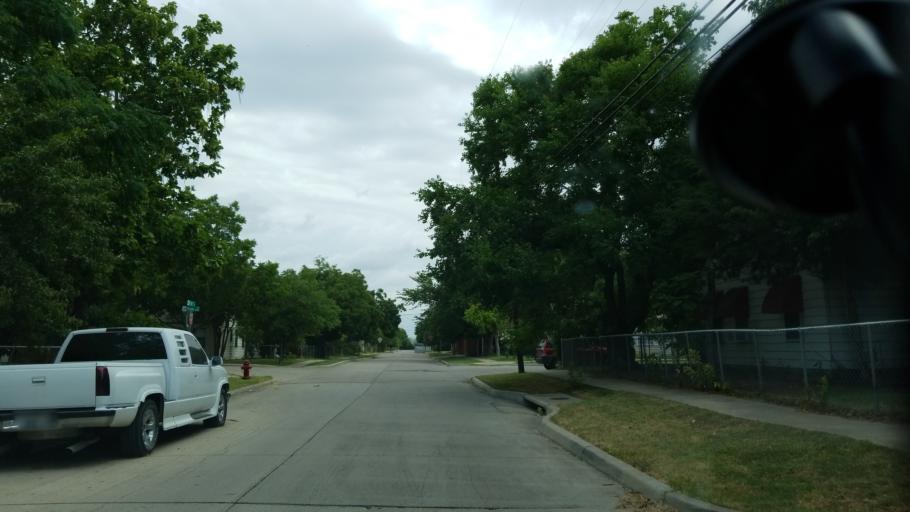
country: US
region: Texas
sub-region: Dallas County
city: Grand Prairie
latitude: 32.7518
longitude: -96.9842
